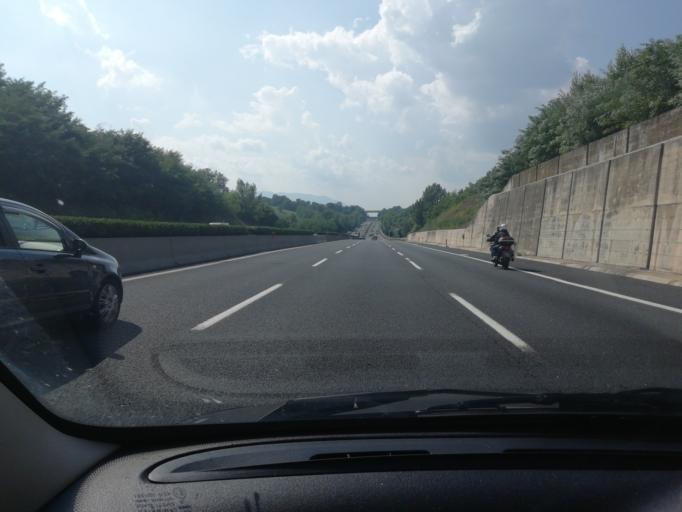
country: IT
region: Latium
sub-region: Provincia di Frosinone
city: Pofi
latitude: 41.5654
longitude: 13.3950
